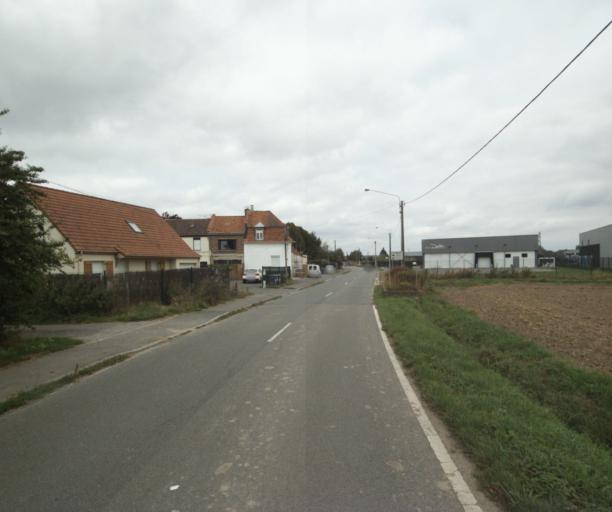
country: FR
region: Nord-Pas-de-Calais
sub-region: Departement du Nord
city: Forest-sur-Marque
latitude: 50.6306
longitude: 3.1938
